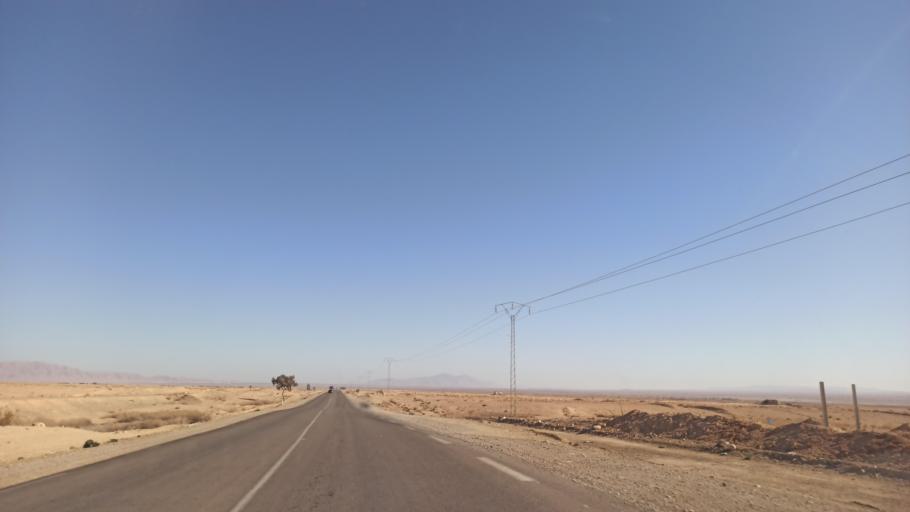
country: TN
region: Gafsa
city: Al Metlaoui
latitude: 34.3139
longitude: 8.4947
